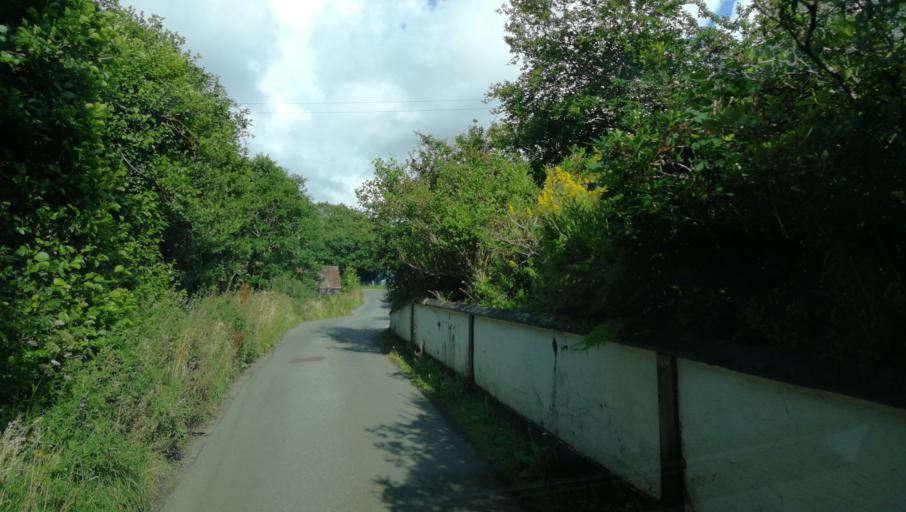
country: GB
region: Scotland
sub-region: Highland
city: Isle of Skye
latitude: 57.4314
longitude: -6.5738
